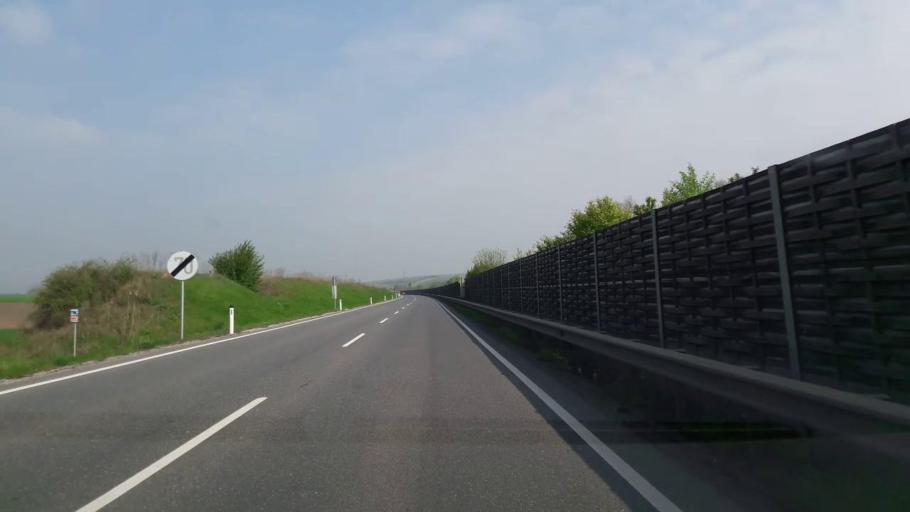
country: AT
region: Lower Austria
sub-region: Politischer Bezirk Hollabrunn
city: Haugsdorf
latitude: 48.7076
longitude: 16.0535
